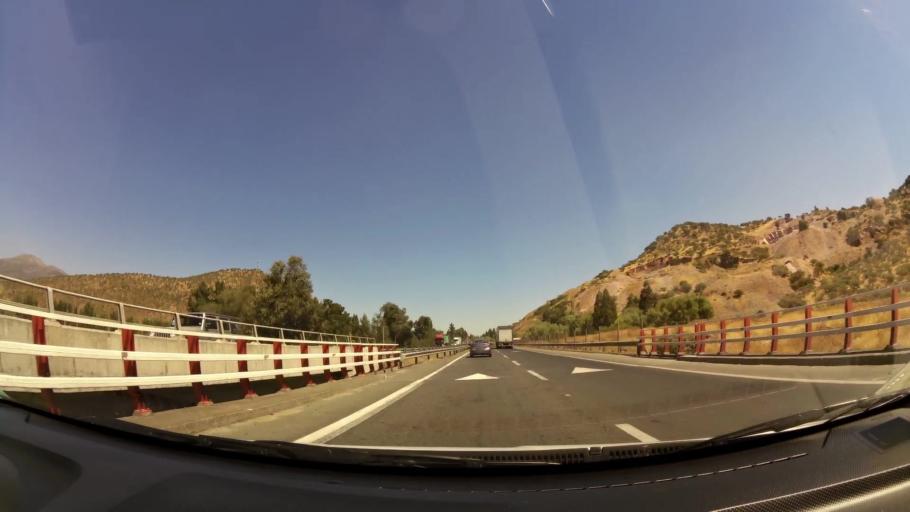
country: CL
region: O'Higgins
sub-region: Provincia de Cachapoal
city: Rengo
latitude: -34.4744
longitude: -70.9004
